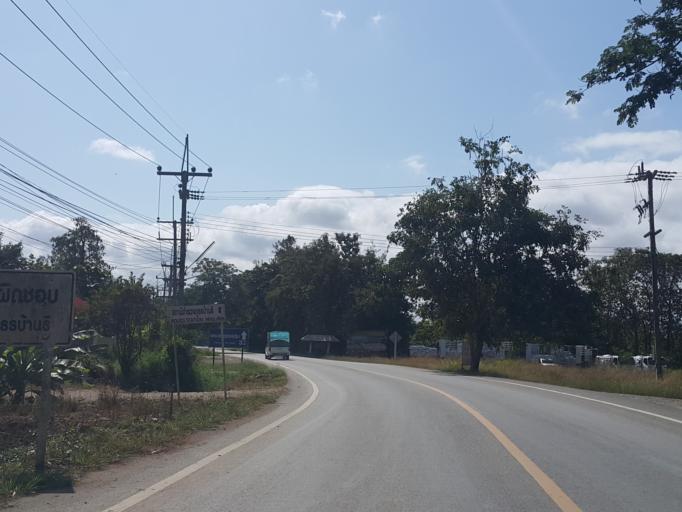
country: TH
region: Chiang Mai
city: San Kamphaeng
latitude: 18.7062
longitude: 99.1657
